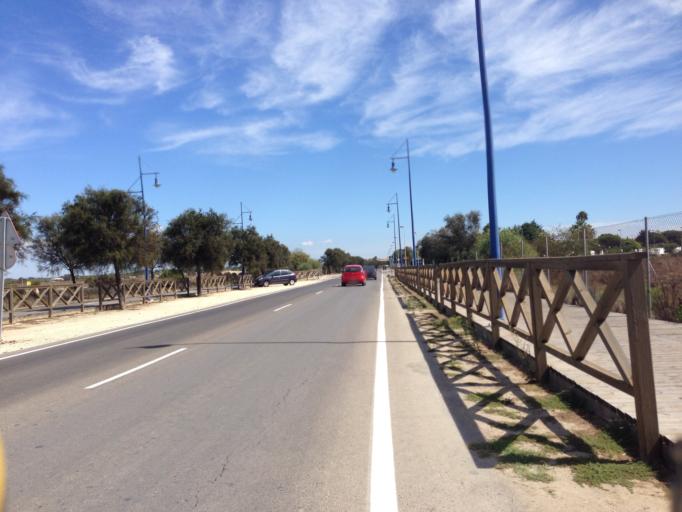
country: ES
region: Andalusia
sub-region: Provincia de Cadiz
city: Chiclana de la Frontera
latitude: 36.3862
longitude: -6.2050
